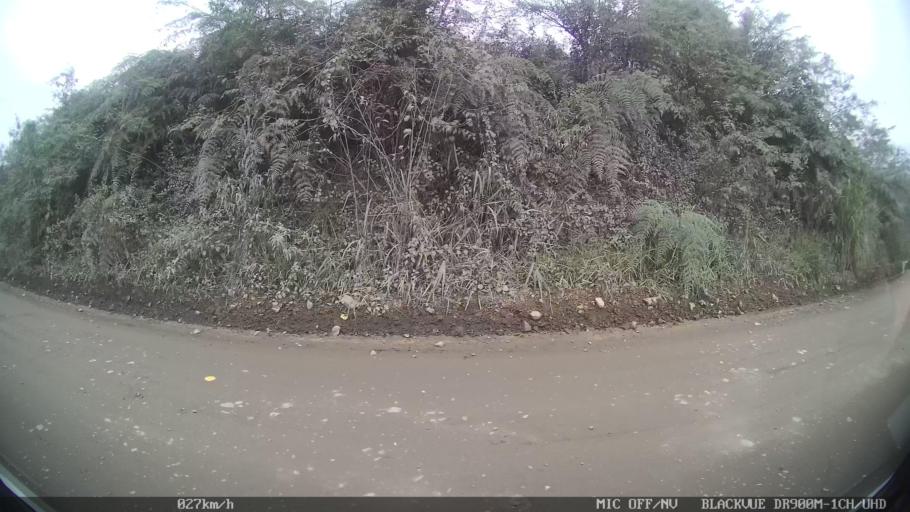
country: BR
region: Santa Catarina
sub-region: Joinville
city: Joinville
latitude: -26.2733
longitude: -48.8920
